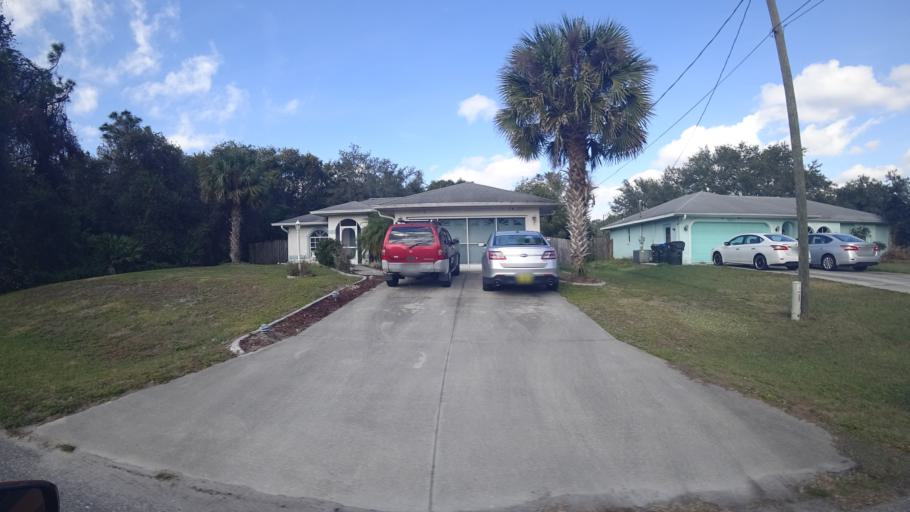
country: US
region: Florida
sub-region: Charlotte County
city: Port Charlotte
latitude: 27.0492
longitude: -82.1225
